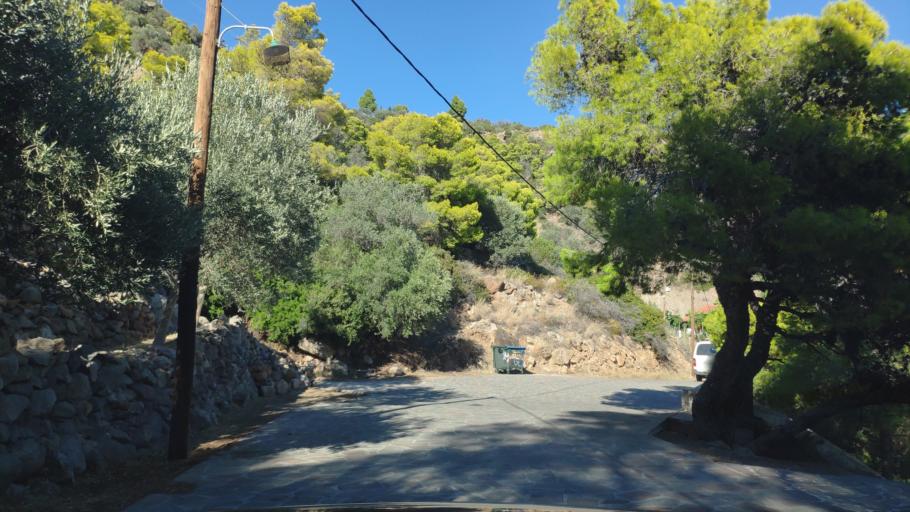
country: GR
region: Attica
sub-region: Nomos Piraios
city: Poros
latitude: 37.5904
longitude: 23.4020
